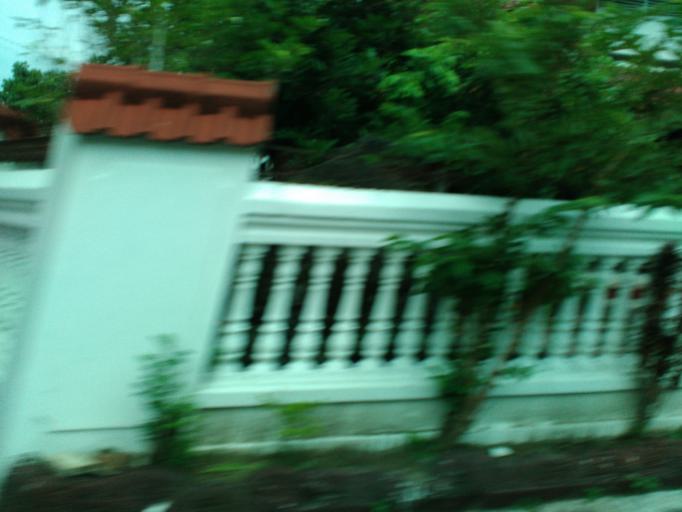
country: ID
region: Central Java
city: Delanggu
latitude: -7.6192
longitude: 110.7011
